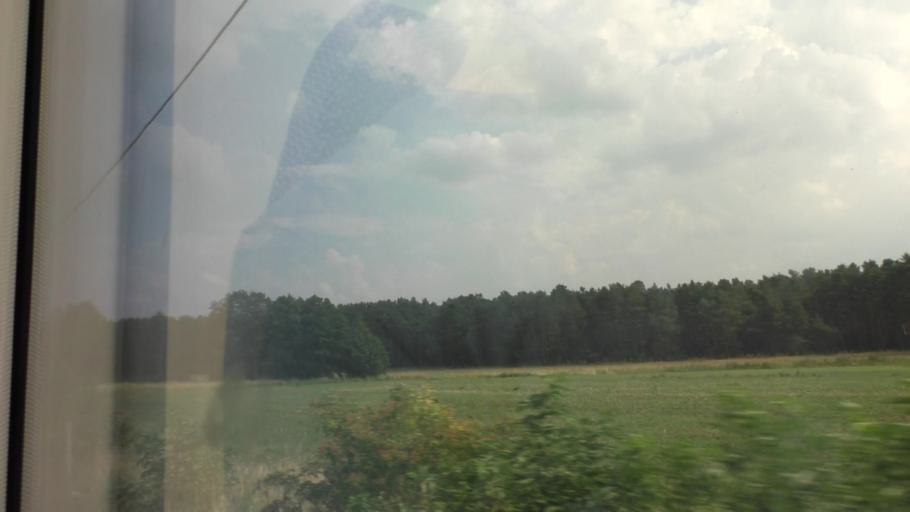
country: DE
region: Brandenburg
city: Spreenhagen
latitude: 52.2838
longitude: 13.8277
